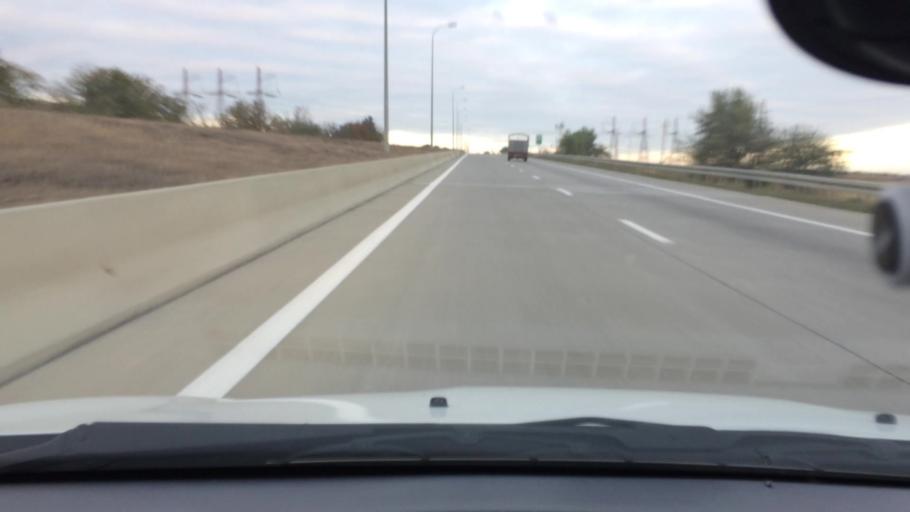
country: GE
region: Shida Kartli
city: Kaspi
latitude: 42.0048
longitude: 44.3617
